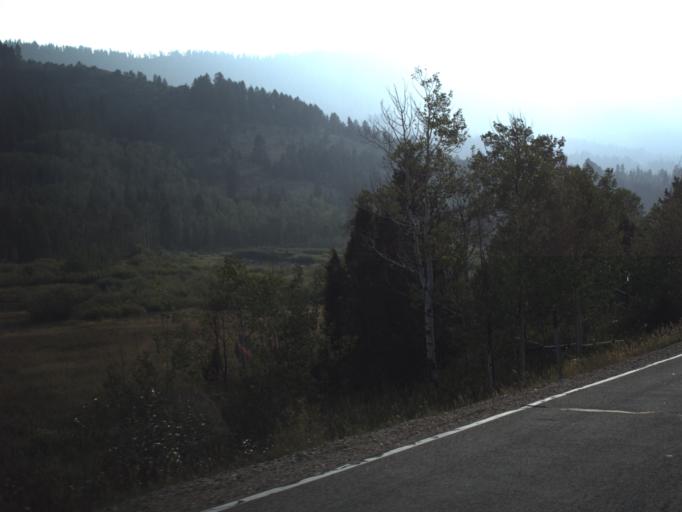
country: US
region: Utah
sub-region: Summit County
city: Francis
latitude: 40.6230
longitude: -111.1469
